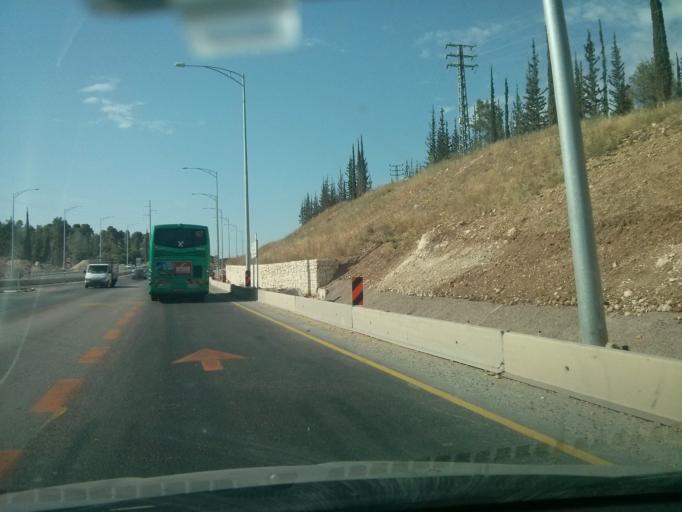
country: IL
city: Mevo horon
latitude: 31.7977
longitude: 35.0146
